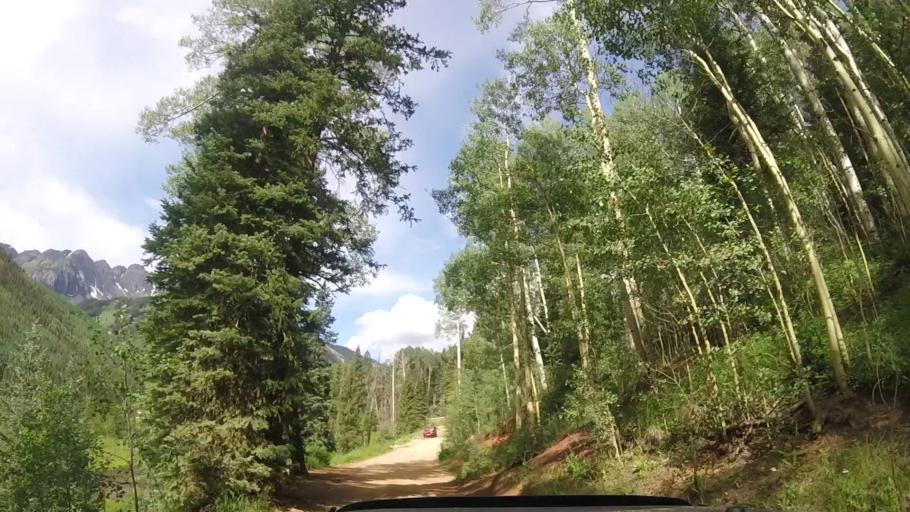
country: US
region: Colorado
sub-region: San Miguel County
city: Telluride
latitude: 37.8576
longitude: -107.8217
